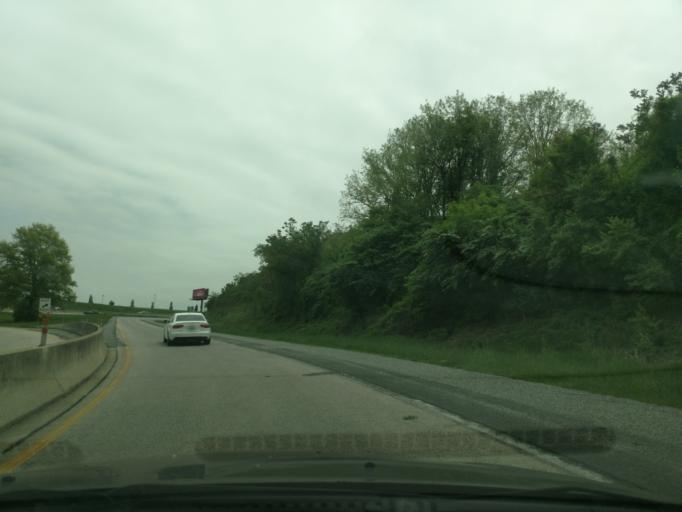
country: US
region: Pennsylvania
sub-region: Berks County
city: Wyomissing
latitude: 40.3363
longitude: -75.9690
